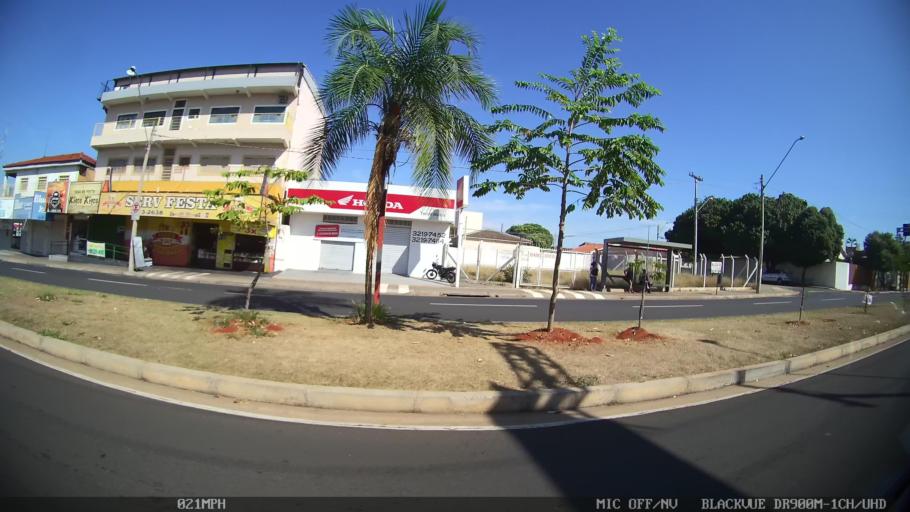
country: BR
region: Sao Paulo
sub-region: Sao Jose Do Rio Preto
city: Sao Jose do Rio Preto
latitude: -20.7844
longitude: -49.3925
